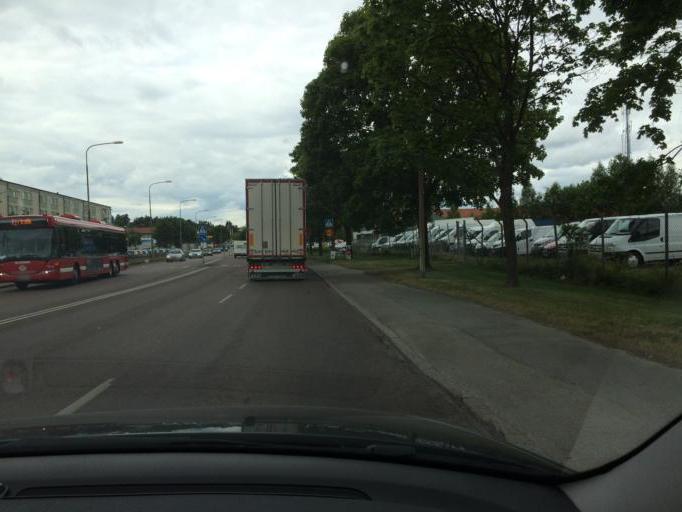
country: SE
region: Stockholm
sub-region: Stockholms Kommun
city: Kista
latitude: 59.3771
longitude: 17.9095
